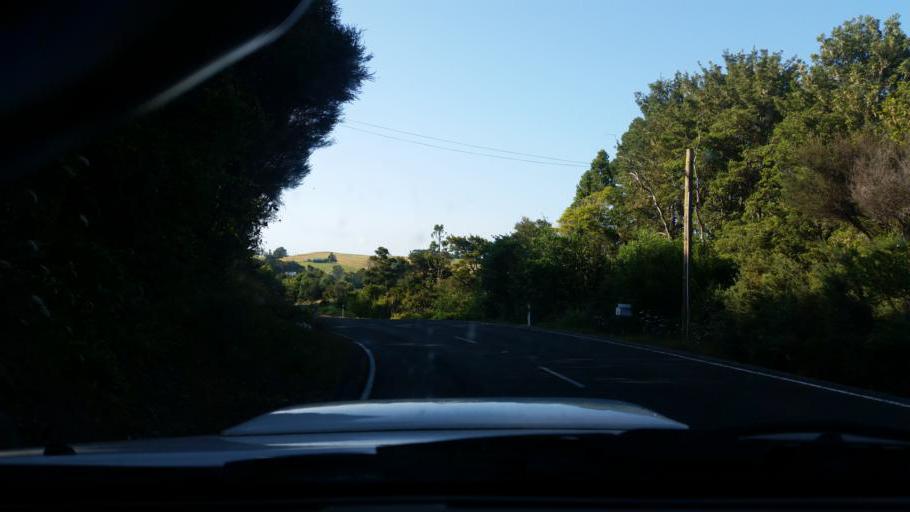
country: NZ
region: Northland
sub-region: Whangarei
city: Ruakaka
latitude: -36.1094
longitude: 174.2294
